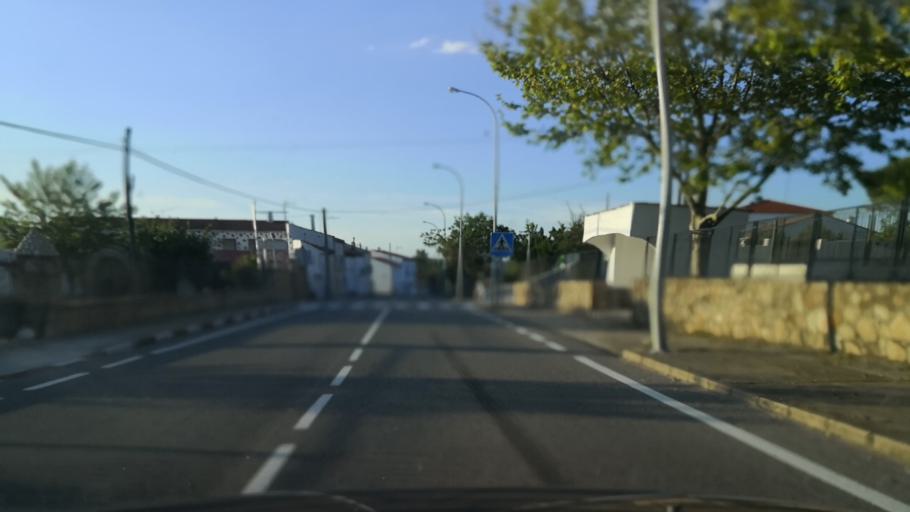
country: PT
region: Portalegre
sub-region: Portalegre
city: Sao Juliao
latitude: 39.3504
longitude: -7.2748
